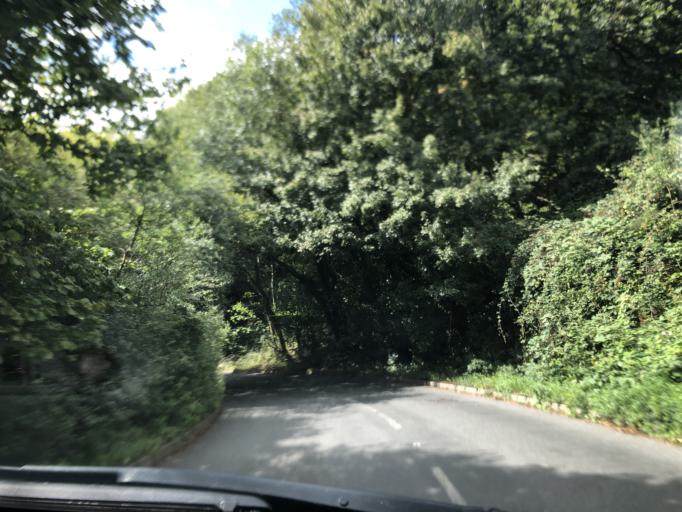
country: GB
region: England
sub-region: Kent
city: Westerham
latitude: 51.2424
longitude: 0.0724
